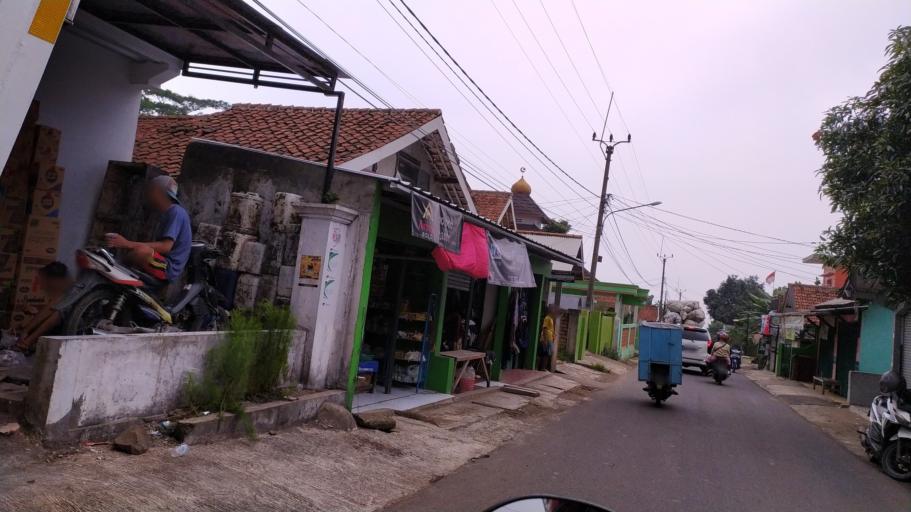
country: ID
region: West Java
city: Ciampea
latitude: -6.5984
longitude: 106.7039
